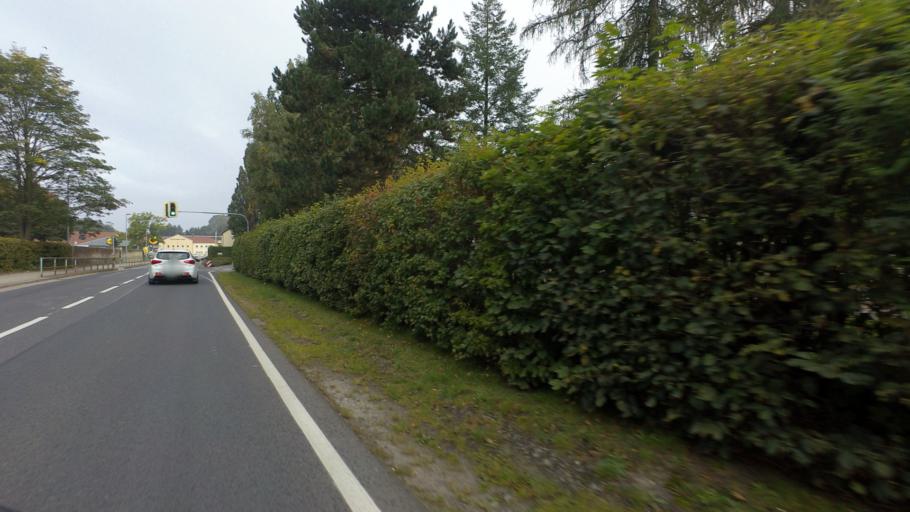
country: DE
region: Saxony
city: Arnsdorf
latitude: 51.0966
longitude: 13.9959
